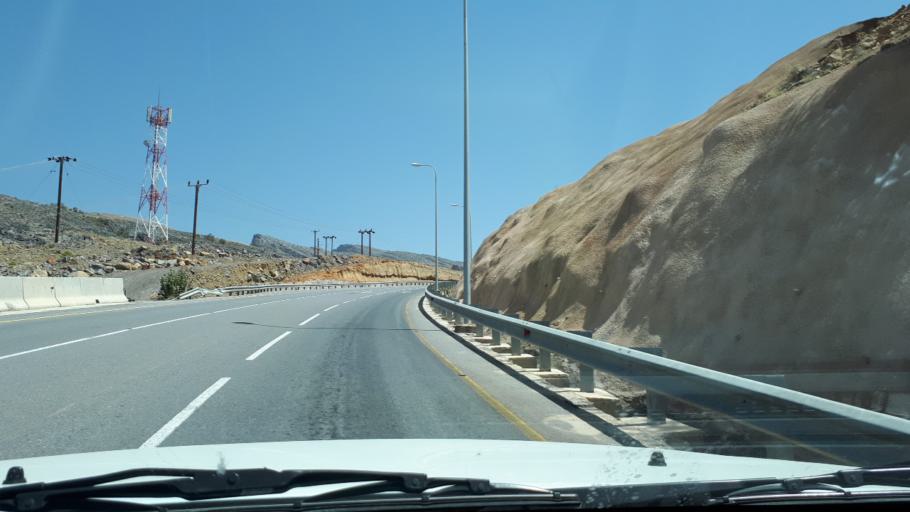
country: OM
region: Muhafazat ad Dakhiliyah
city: Izki
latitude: 22.9922
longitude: 57.7006
